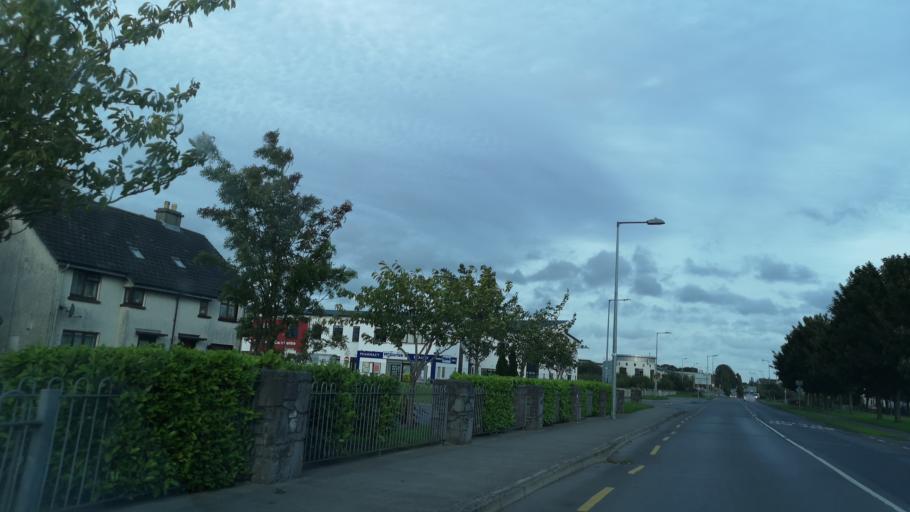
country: IE
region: Leinster
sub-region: An Iarmhi
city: Athlone
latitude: 53.4332
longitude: -7.9438
